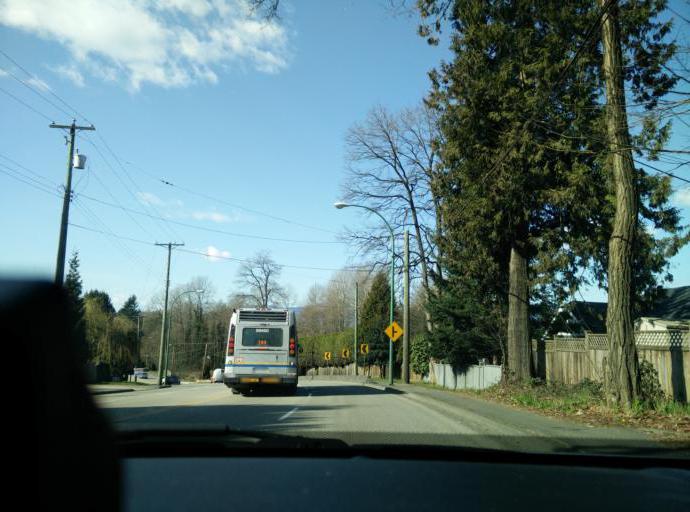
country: CA
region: British Columbia
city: Burnaby
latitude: 49.2375
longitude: -122.9567
